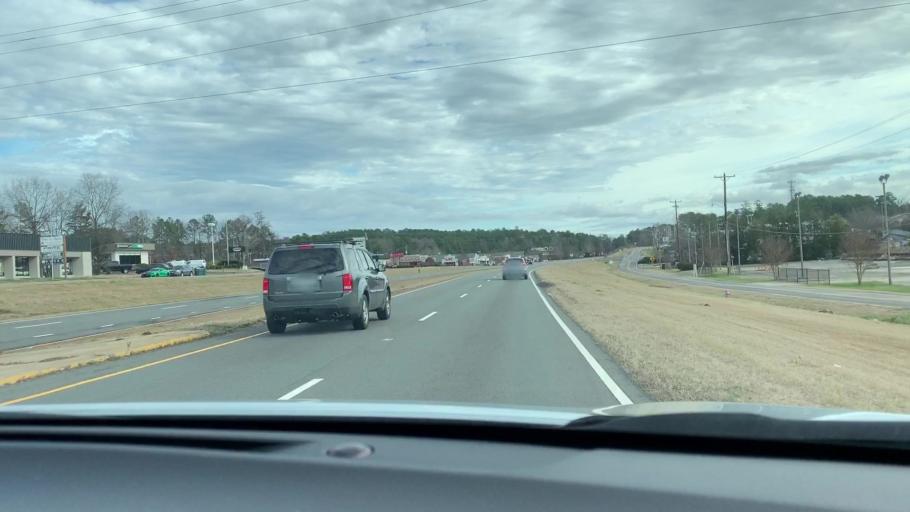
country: US
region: North Carolina
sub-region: Durham County
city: Durham
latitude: 35.9706
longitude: -78.9537
